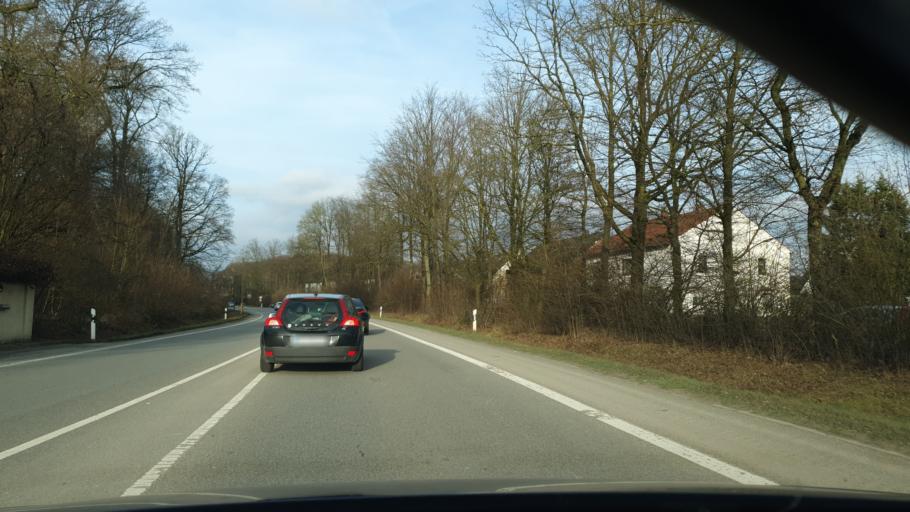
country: DE
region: North Rhine-Westphalia
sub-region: Regierungsbezirk Detmold
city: Bielefeld
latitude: 52.0812
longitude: 8.5165
